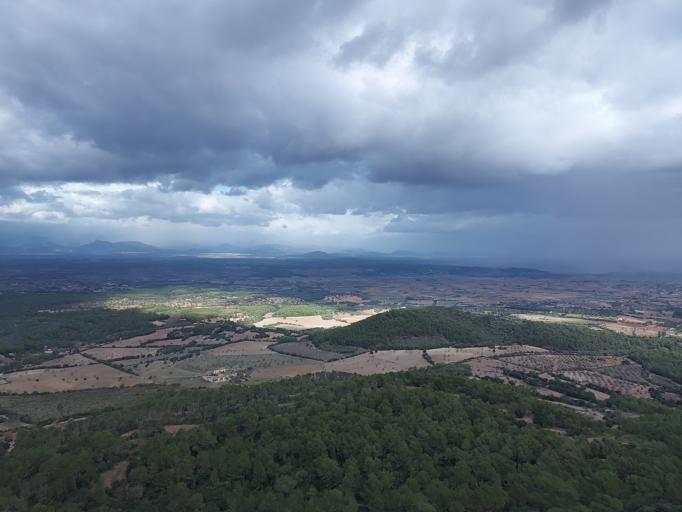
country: ES
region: Balearic Islands
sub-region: Illes Balears
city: Algaida
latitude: 39.5273
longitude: 2.9286
